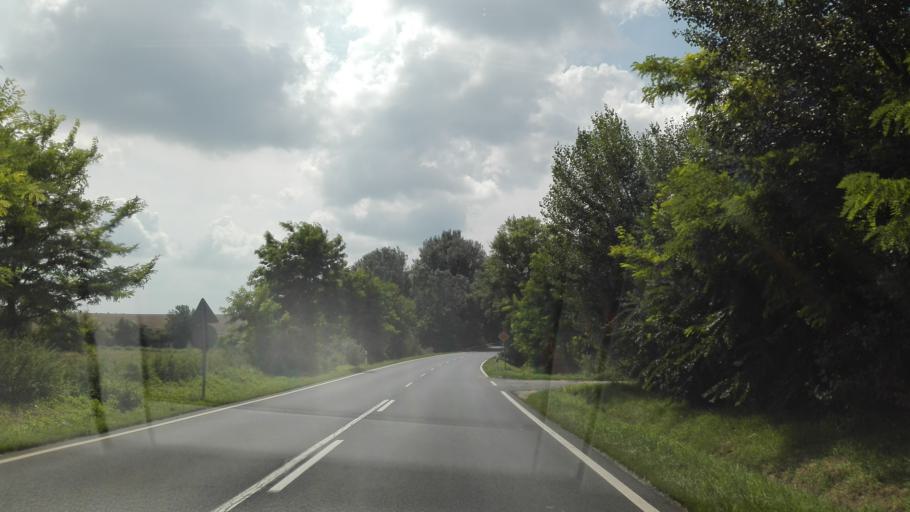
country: HU
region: Fejer
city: Eloszallas
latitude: 46.8106
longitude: 18.7777
